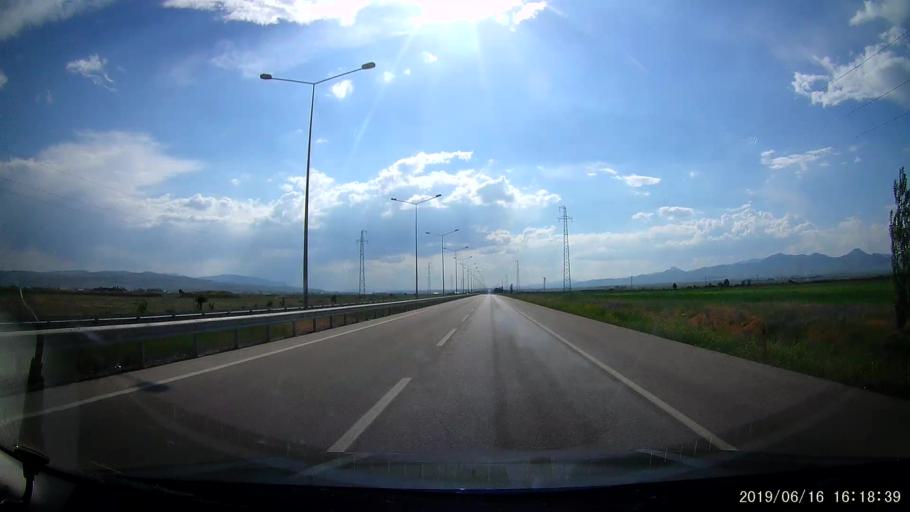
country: TR
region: Erzurum
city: Ilica
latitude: 39.9650
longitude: 41.1628
